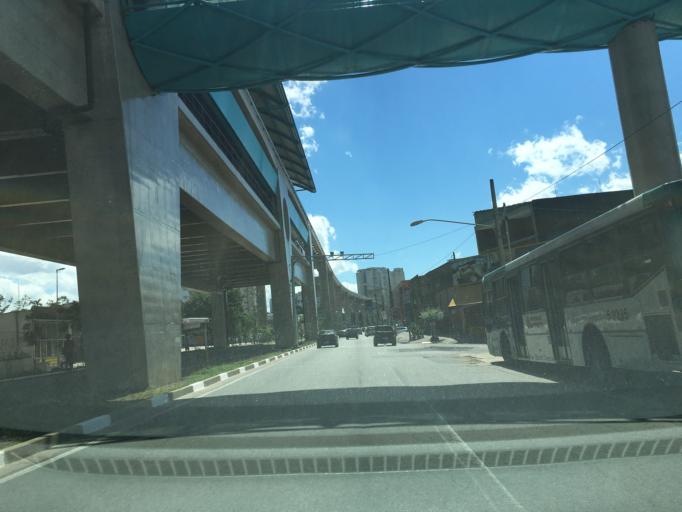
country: BR
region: Sao Paulo
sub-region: Sao Caetano Do Sul
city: Sao Caetano do Sul
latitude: -23.5820
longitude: -46.5617
